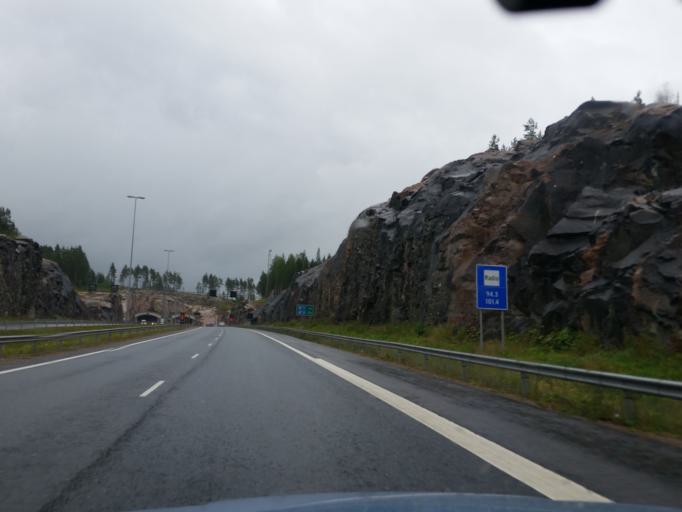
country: FI
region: Varsinais-Suomi
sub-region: Salo
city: Muurla
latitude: 60.3774
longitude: 23.3272
